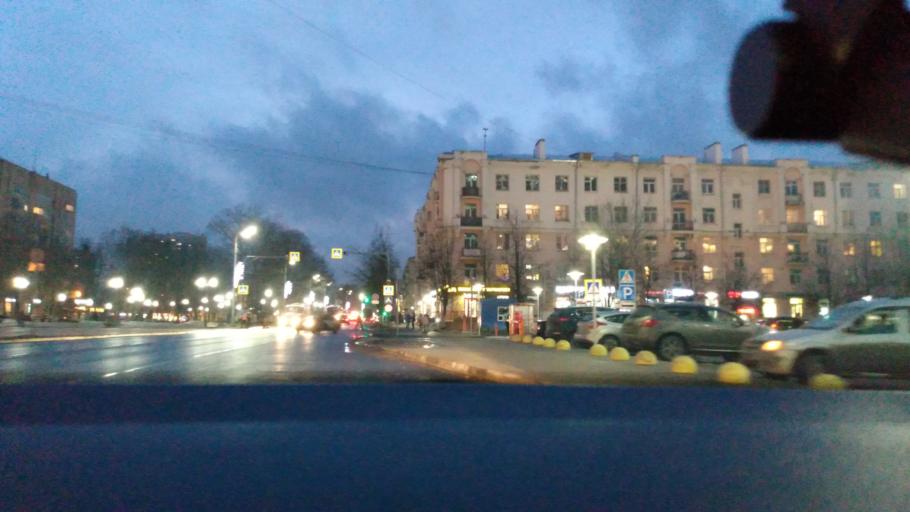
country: RU
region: Moskovskaya
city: Balashikha
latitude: 55.7973
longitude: 37.9388
